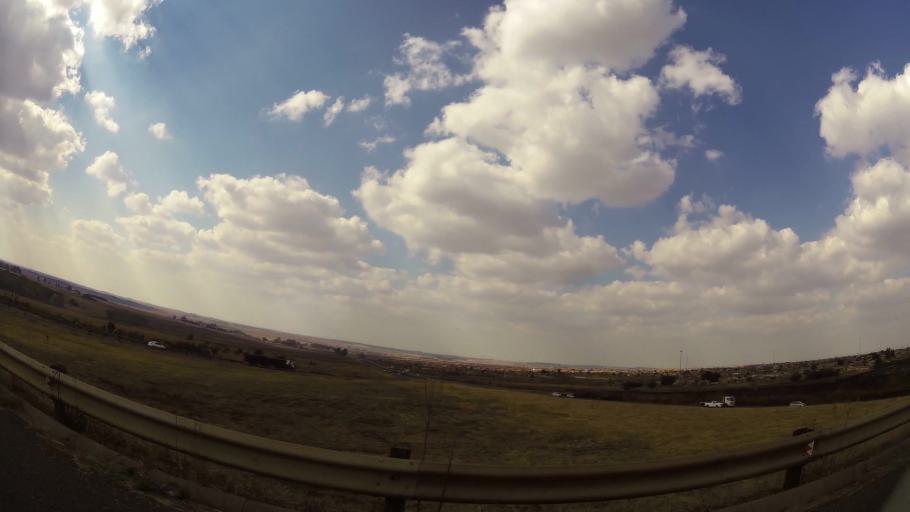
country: ZA
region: Mpumalanga
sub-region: Nkangala District Municipality
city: Delmas
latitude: -26.0914
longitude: 28.6771
